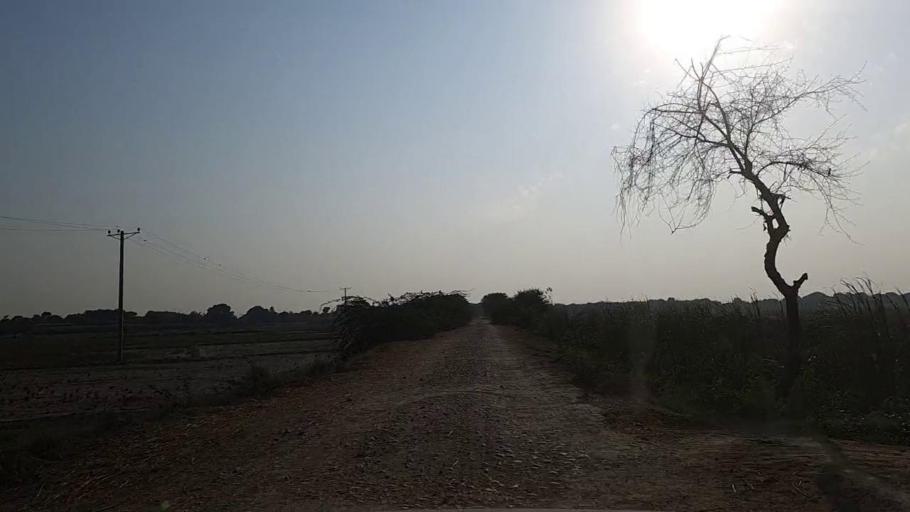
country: PK
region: Sindh
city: Mirpur Batoro
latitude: 24.7870
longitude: 68.2485
